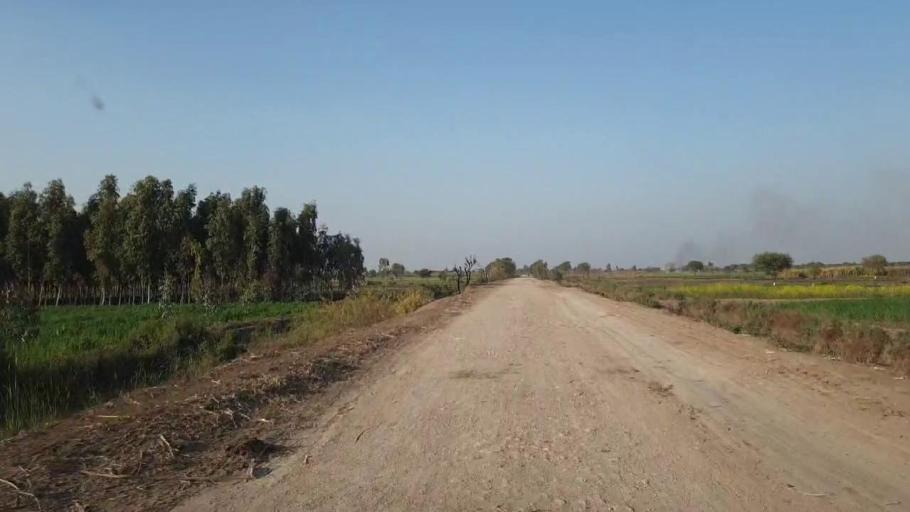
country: PK
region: Sindh
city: Chambar
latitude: 25.3416
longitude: 68.7059
